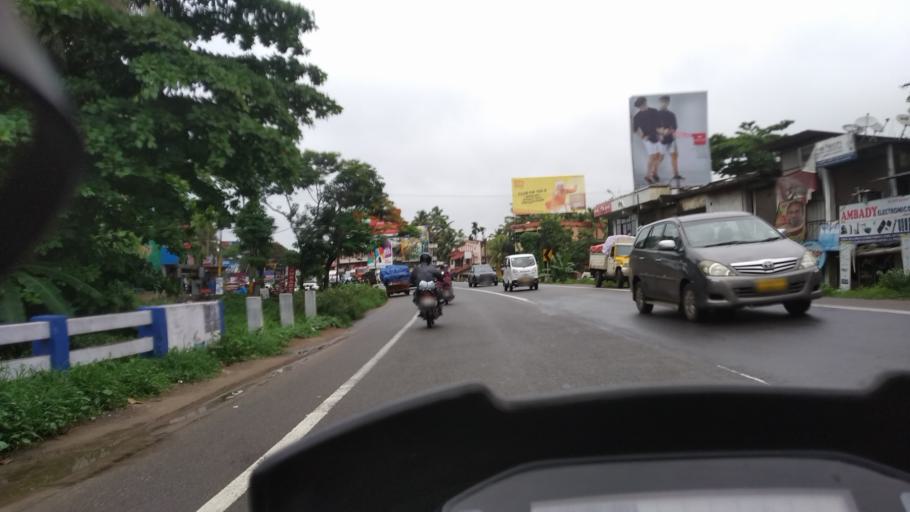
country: IN
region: Kerala
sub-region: Alappuzha
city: Mavelikara
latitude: 9.2808
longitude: 76.4583
